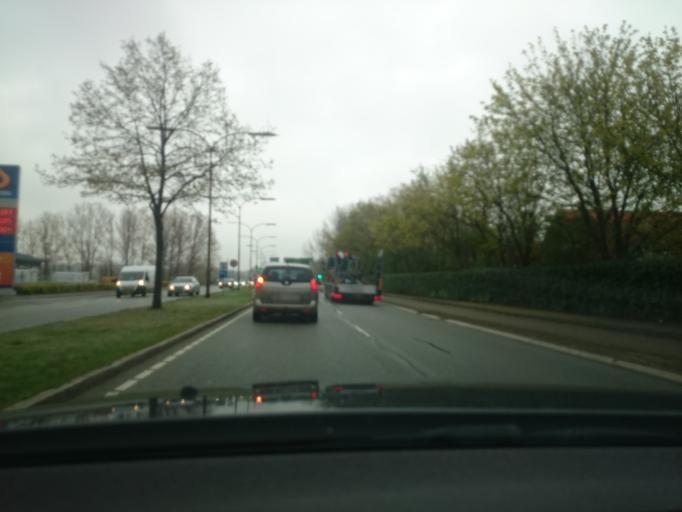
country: DK
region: Capital Region
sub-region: Lyngby-Tarbaek Kommune
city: Kongens Lyngby
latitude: 55.7747
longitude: 12.5205
